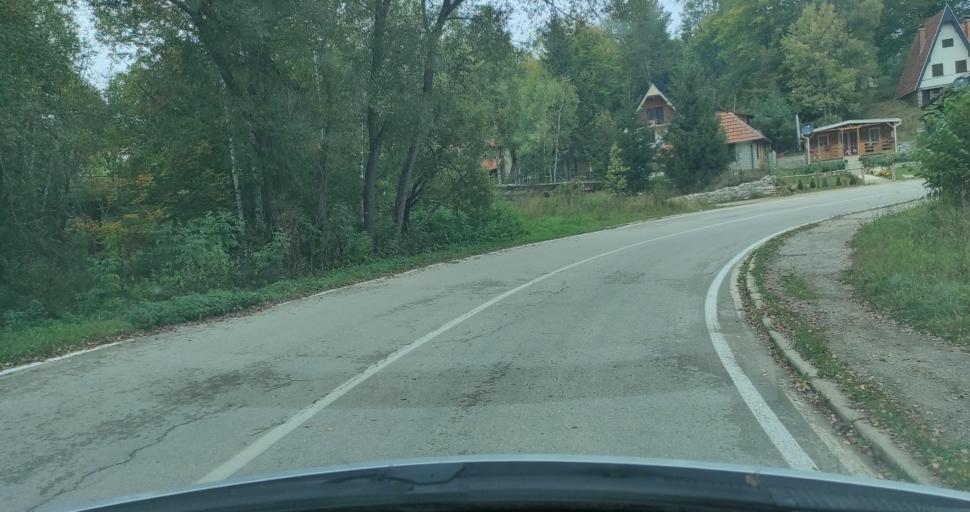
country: RS
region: Central Serbia
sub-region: Jablanicki Okrug
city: Crna Trava
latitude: 42.7458
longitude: 22.3227
